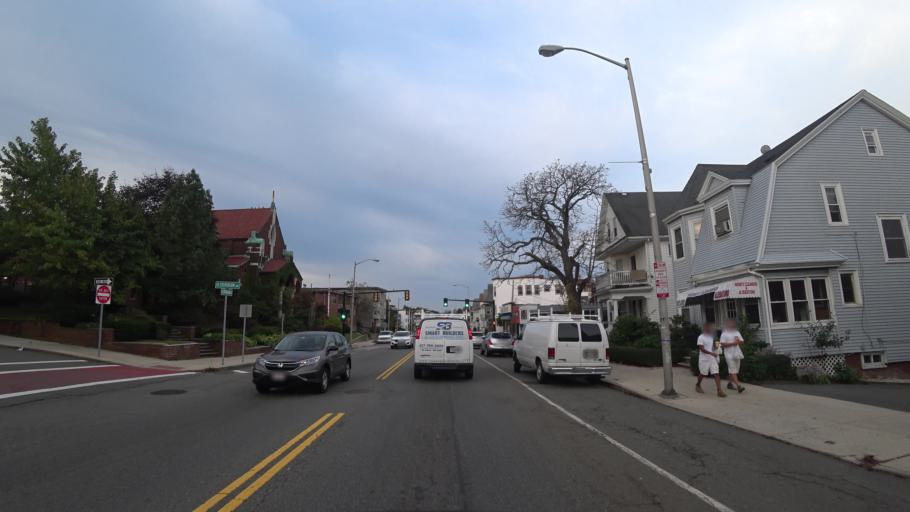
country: US
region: Massachusetts
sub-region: Middlesex County
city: Everett
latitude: 42.4178
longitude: -71.0460
